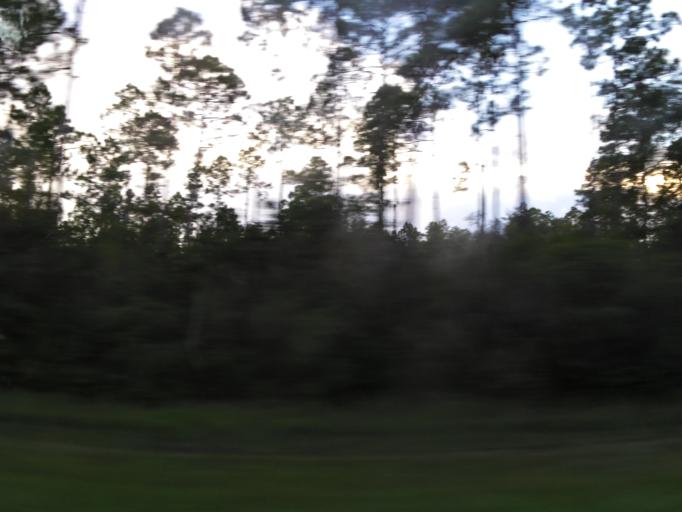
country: US
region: Georgia
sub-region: Echols County
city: Statenville
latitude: 30.7188
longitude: -83.0695
